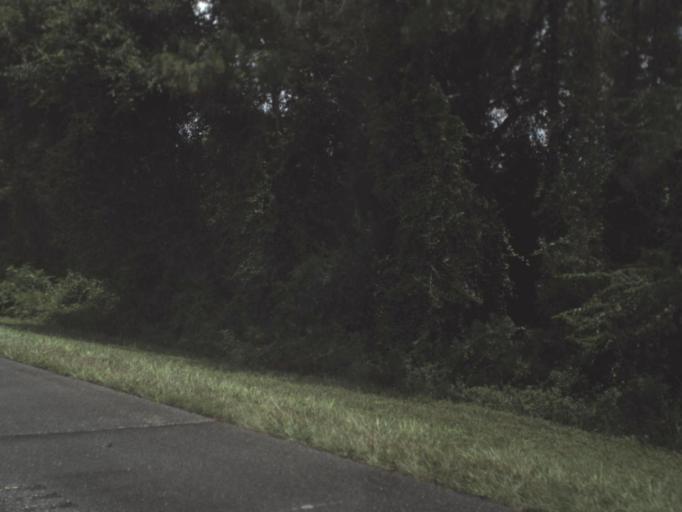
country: US
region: Florida
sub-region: Hernando County
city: Hill 'n Dale
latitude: 28.5353
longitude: -82.2369
